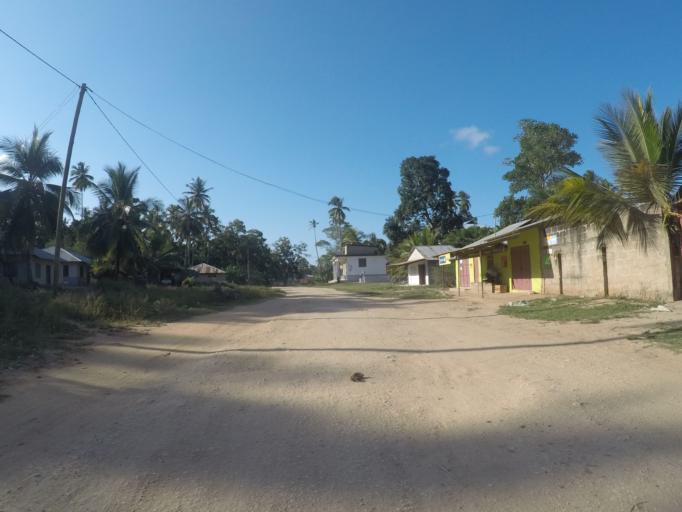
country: TZ
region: Zanzibar Central/South
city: Koani
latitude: -6.1571
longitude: 39.2873
